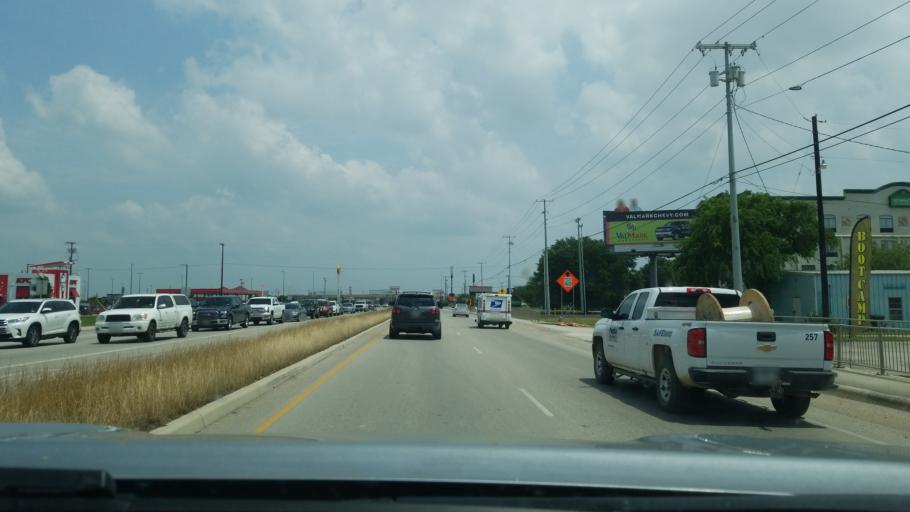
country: US
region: Texas
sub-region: Comal County
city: New Braunfels
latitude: 29.7318
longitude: -98.0817
